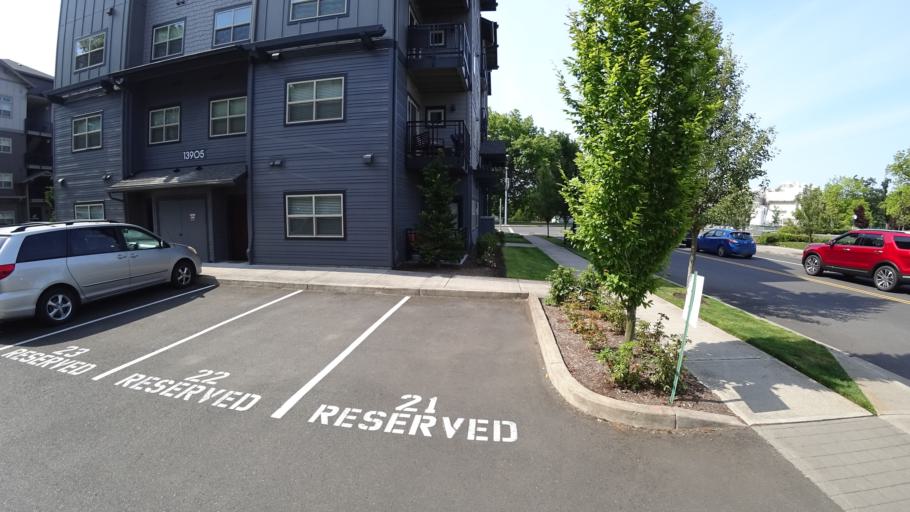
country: US
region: Oregon
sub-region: Washington County
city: Cedar Hills
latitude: 45.5032
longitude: -122.8218
